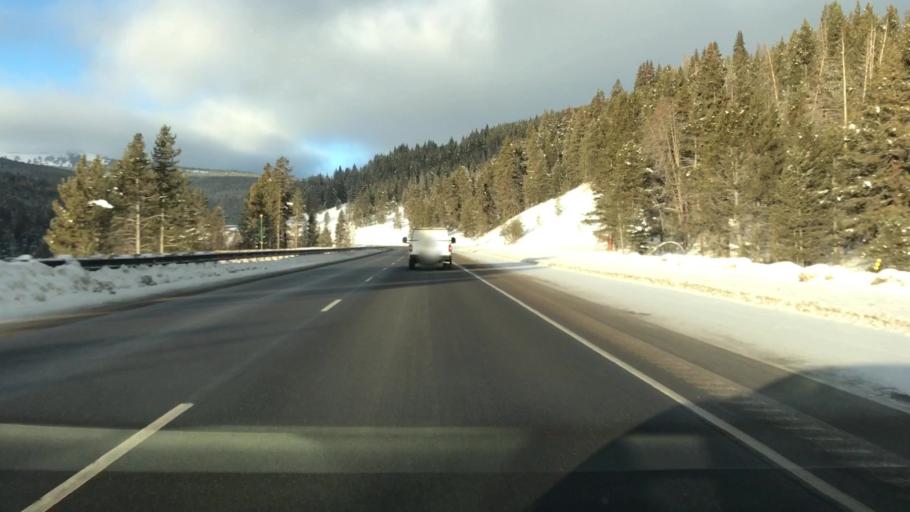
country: US
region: Colorado
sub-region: Summit County
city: Frisco
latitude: 39.5066
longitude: -106.1866
